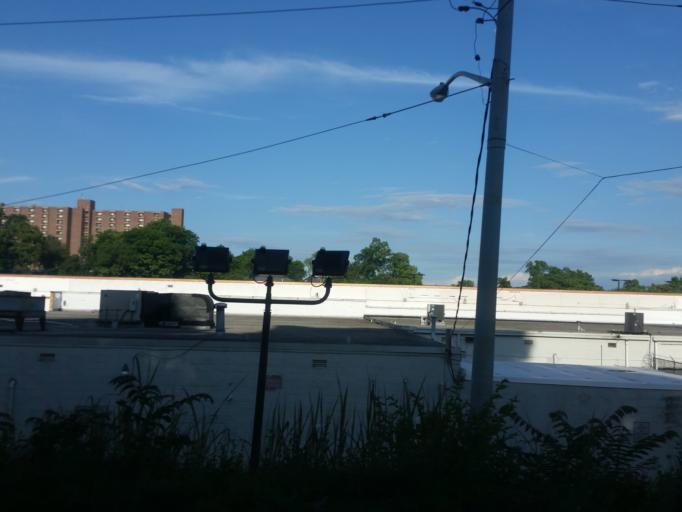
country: US
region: Tennessee
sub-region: Knox County
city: Knoxville
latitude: 35.9917
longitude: -83.9226
